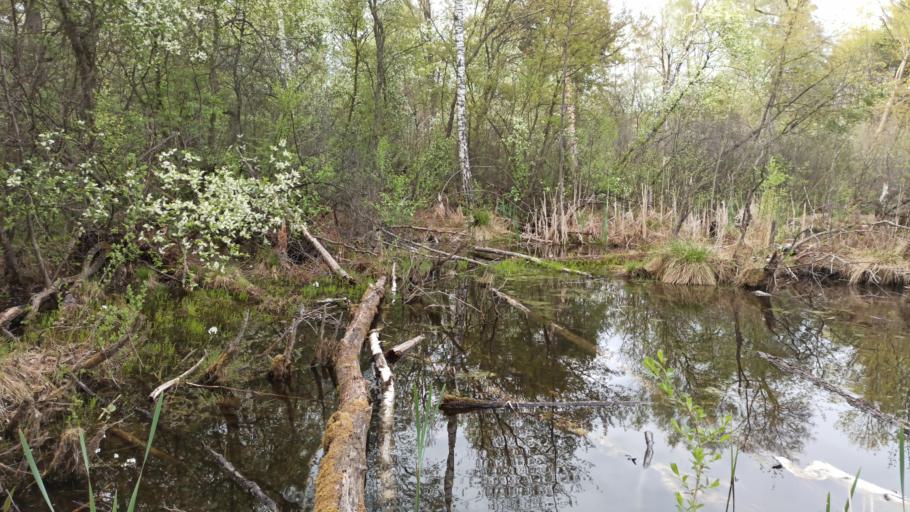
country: PL
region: Masovian Voivodeship
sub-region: Powiat otwocki
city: Karczew
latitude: 52.0737
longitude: 21.2843
